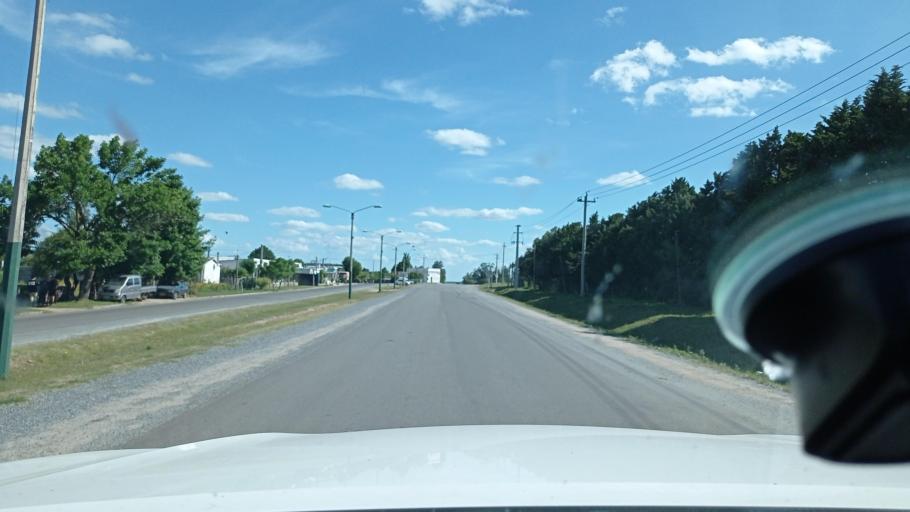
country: UY
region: Florida
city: Florida
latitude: -34.0893
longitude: -56.2383
